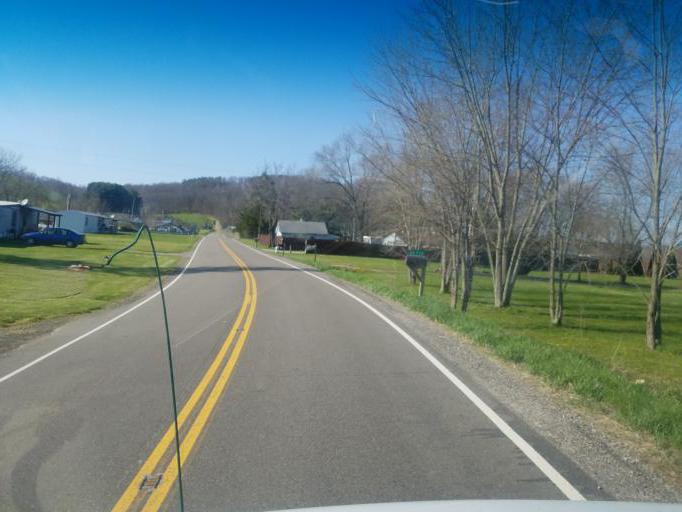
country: US
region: Ohio
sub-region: Knox County
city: Oak Hill
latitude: 40.3186
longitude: -82.0792
